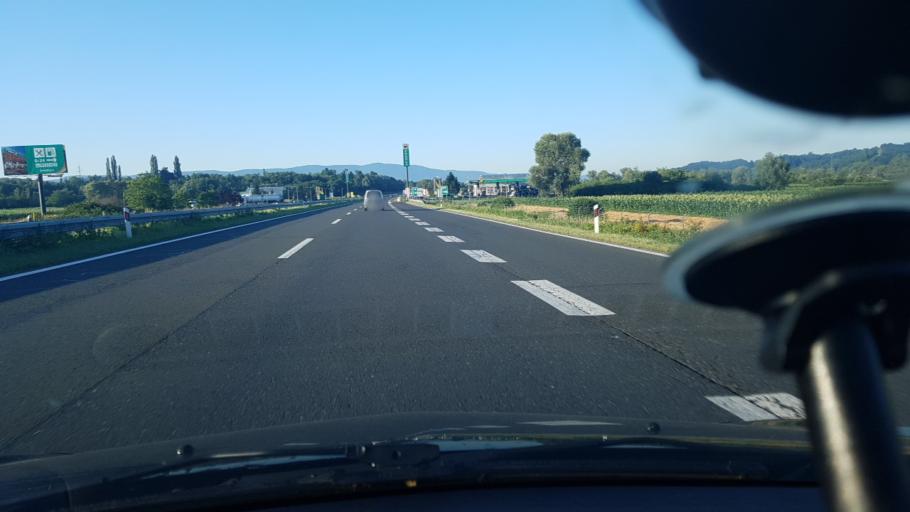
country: HR
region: Krapinsko-Zagorska
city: Zabok
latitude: 46.0701
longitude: 15.9190
